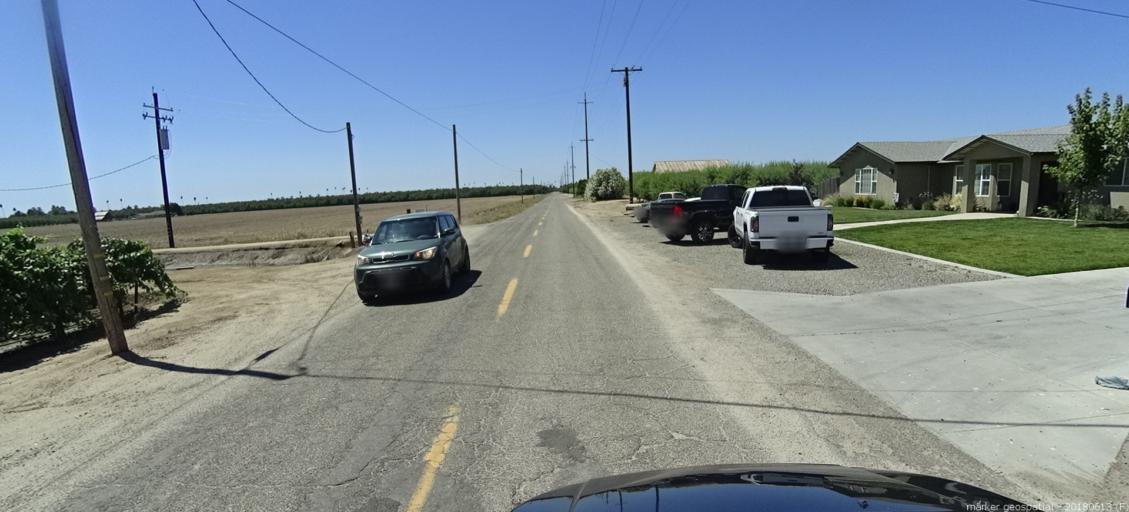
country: US
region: California
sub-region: Madera County
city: Chowchilla
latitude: 37.0799
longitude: -120.3103
